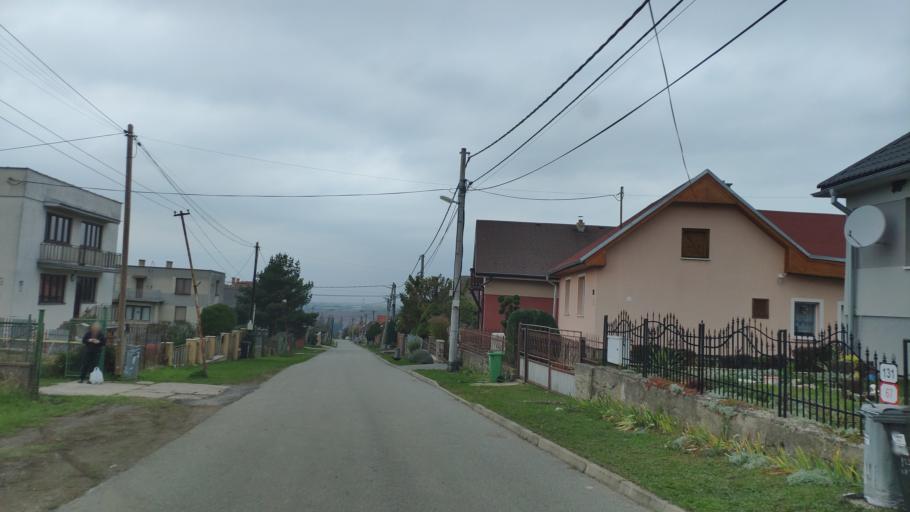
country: SK
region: Kosicky
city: Kosice
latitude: 48.6353
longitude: 21.3900
